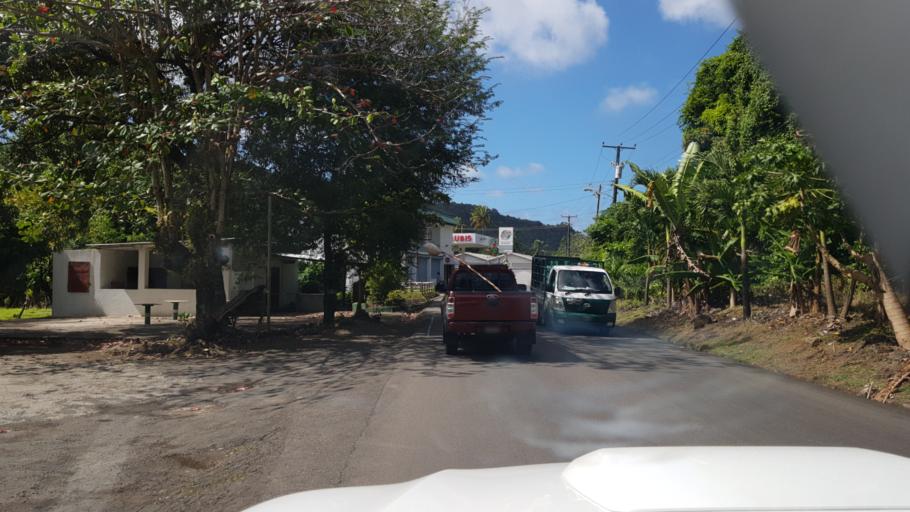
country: LC
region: Castries Quarter
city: Bisee
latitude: 14.0167
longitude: -60.9580
